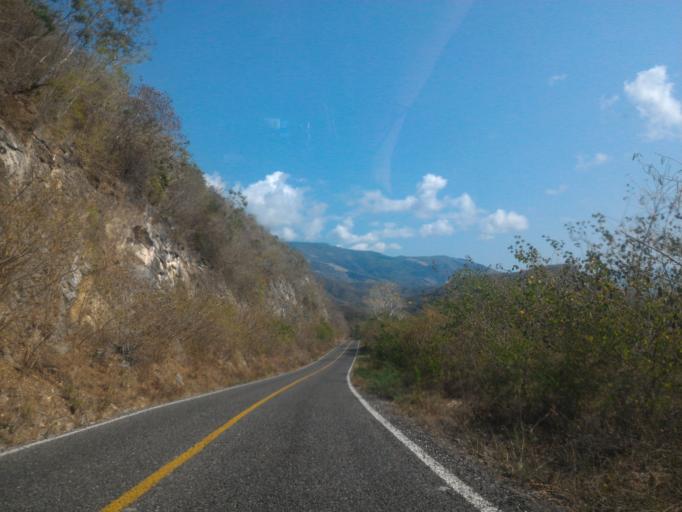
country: MX
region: Michoacan
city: Coahuayana Viejo
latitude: 18.4650
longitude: -103.5503
